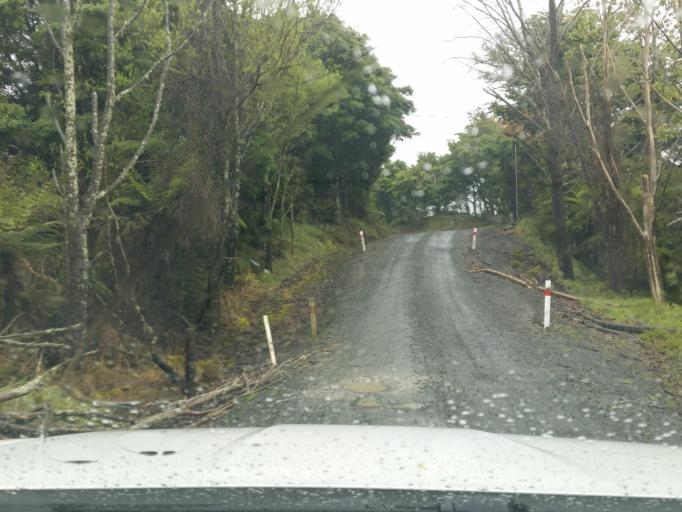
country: NZ
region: Northland
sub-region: Kaipara District
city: Dargaville
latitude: -35.7691
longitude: 173.9617
